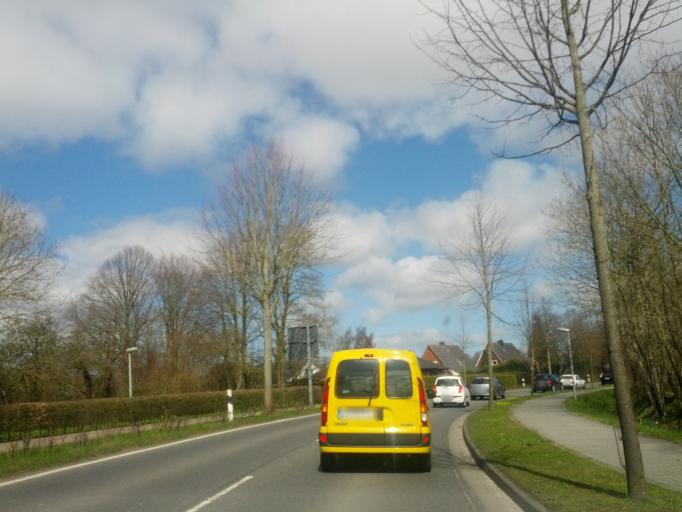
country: DE
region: Lower Saxony
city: Esens
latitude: 53.6458
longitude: 7.6069
